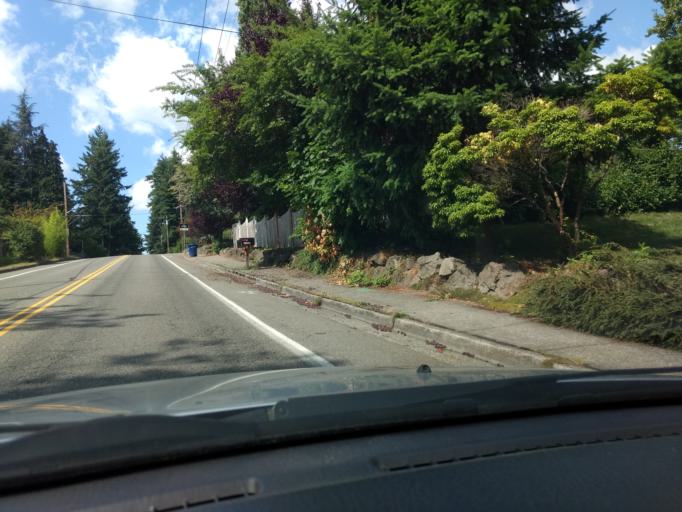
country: US
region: Washington
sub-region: King County
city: Bothell
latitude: 47.7622
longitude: -122.2017
